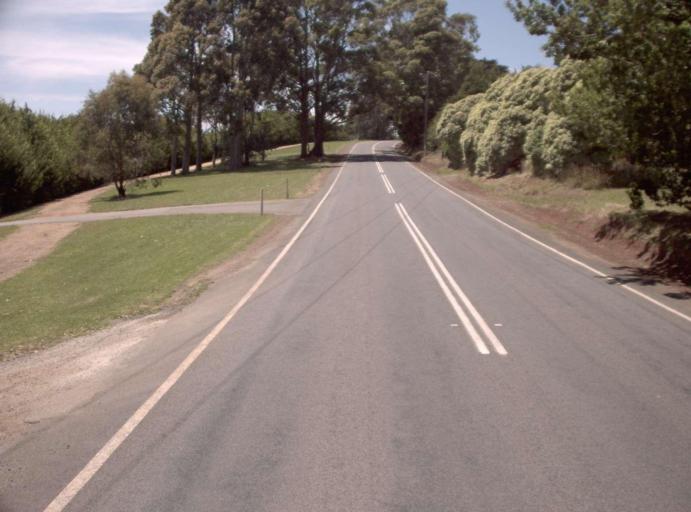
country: AU
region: Victoria
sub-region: Baw Baw
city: Warragul
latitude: -37.9757
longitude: 145.9469
